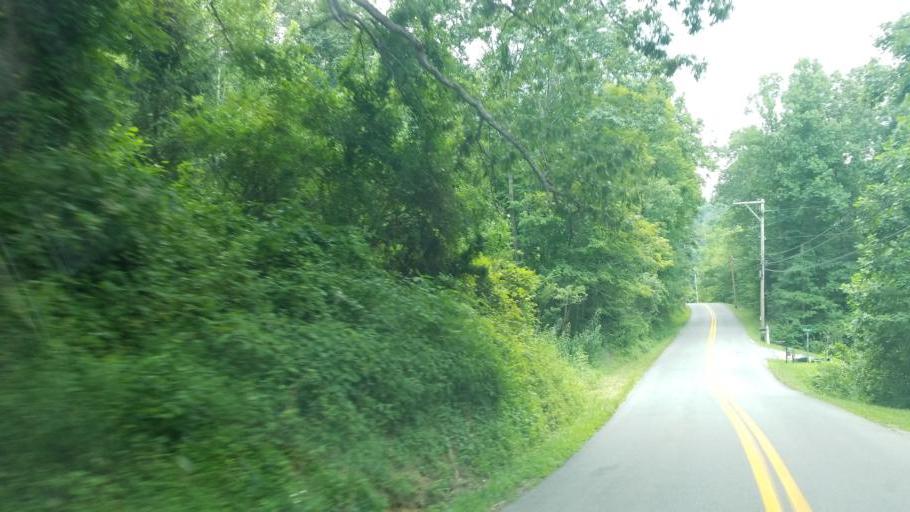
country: US
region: West Virginia
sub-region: Kanawha County
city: Alum Creek
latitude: 38.2949
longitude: -81.7872
